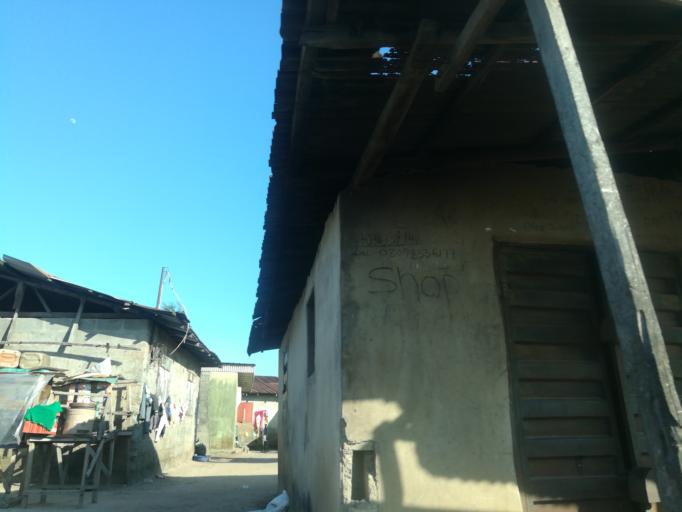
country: NG
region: Lagos
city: Ikorodu
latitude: 6.5376
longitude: 3.5520
